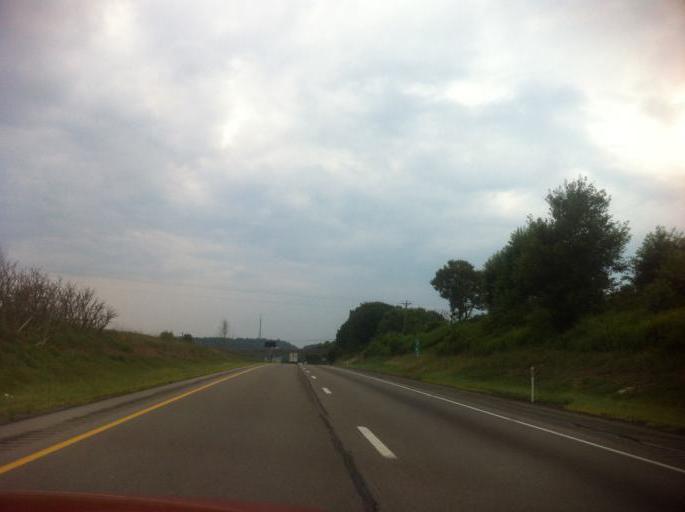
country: US
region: Pennsylvania
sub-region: Jefferson County
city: Brookville
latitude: 41.1812
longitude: -79.1430
